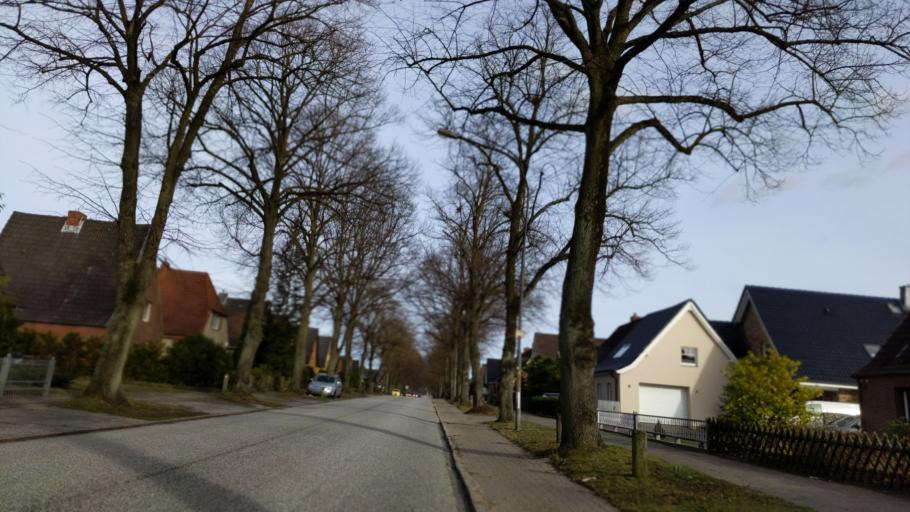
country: DE
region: Mecklenburg-Vorpommern
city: Selmsdorf
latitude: 53.9127
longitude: 10.8134
